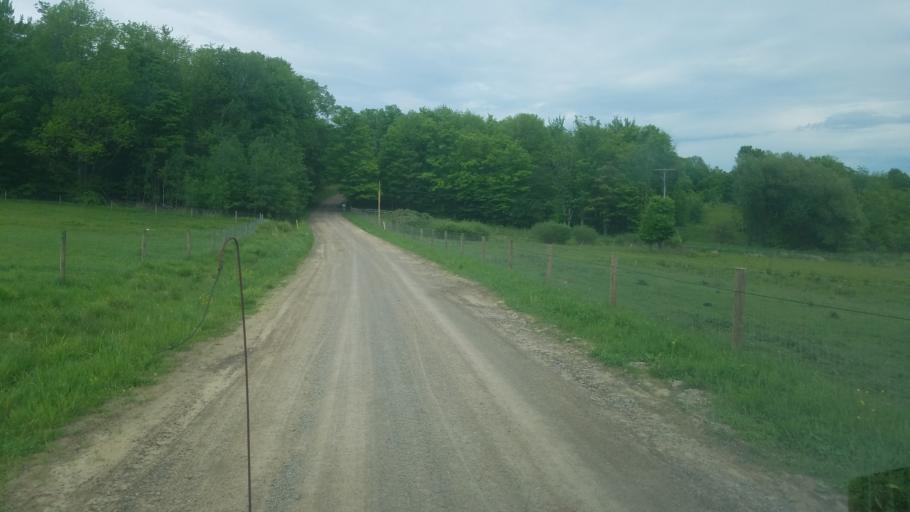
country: US
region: Pennsylvania
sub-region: Tioga County
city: Westfield
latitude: 41.9290
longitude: -77.7016
